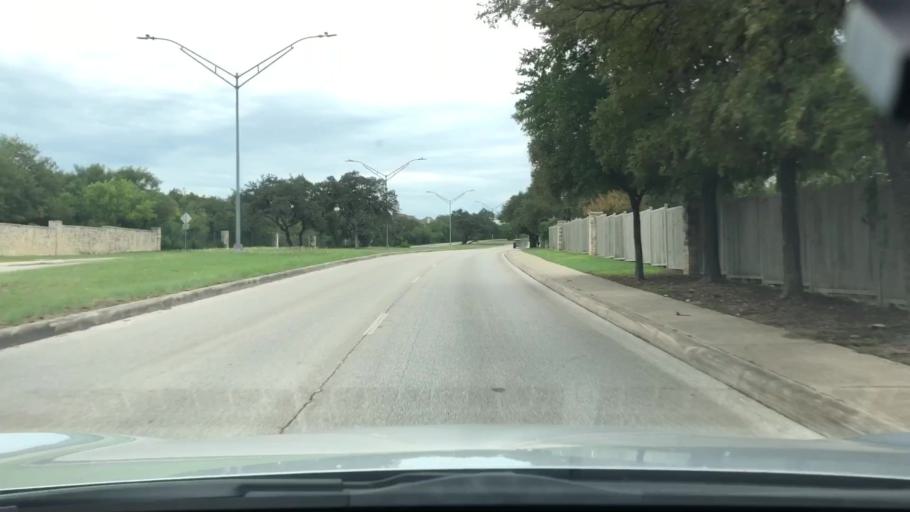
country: US
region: Texas
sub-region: Bexar County
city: Leon Valley
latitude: 29.4616
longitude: -98.6730
